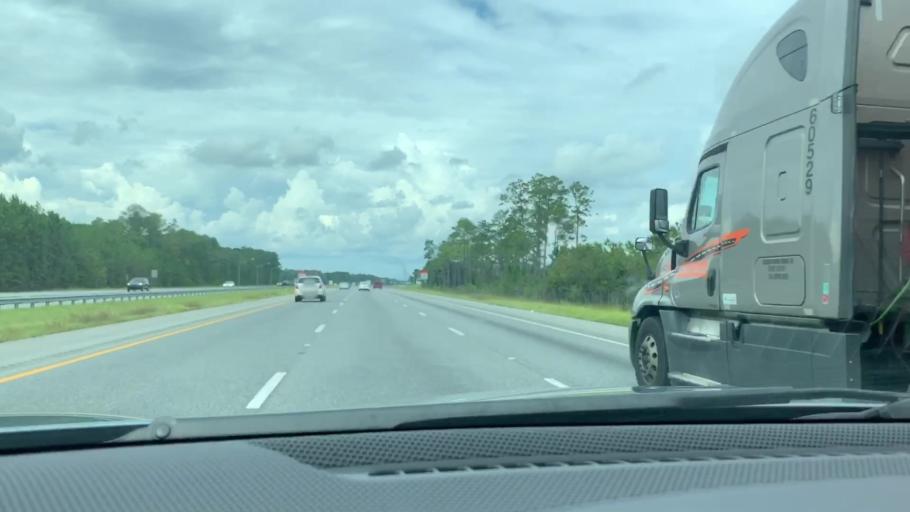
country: US
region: Georgia
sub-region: McIntosh County
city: Darien
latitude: 31.4693
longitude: -81.4466
